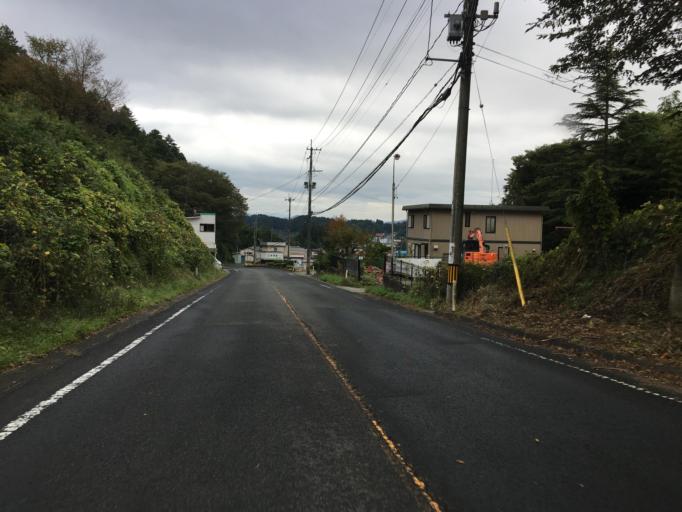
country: JP
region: Fukushima
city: Nihommatsu
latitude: 37.6106
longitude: 140.4438
